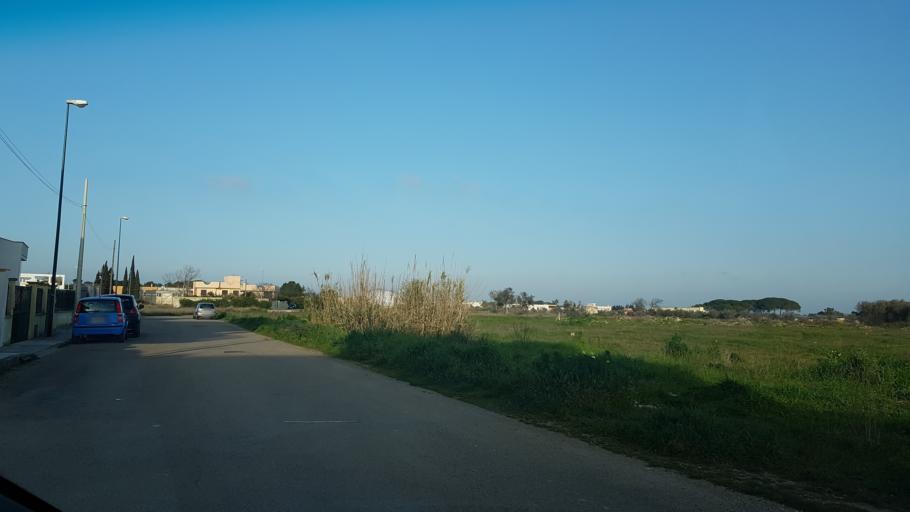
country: IT
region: Apulia
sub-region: Provincia di Lecce
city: Campi Salentina
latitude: 40.3926
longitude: 18.0244
